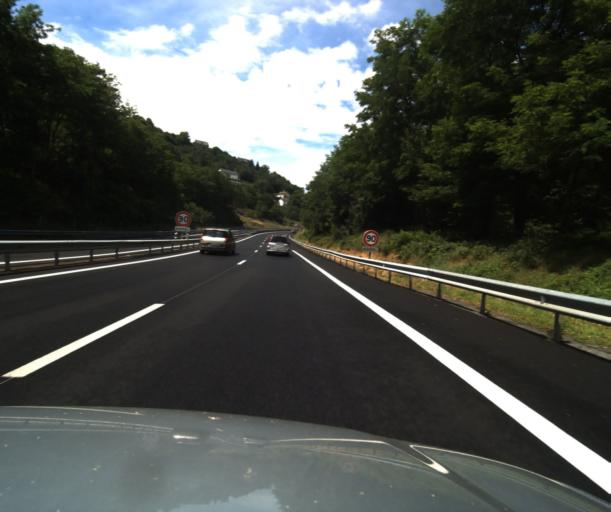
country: FR
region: Midi-Pyrenees
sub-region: Departement des Hautes-Pyrenees
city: Lourdes
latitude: 43.0683
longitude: -0.0423
